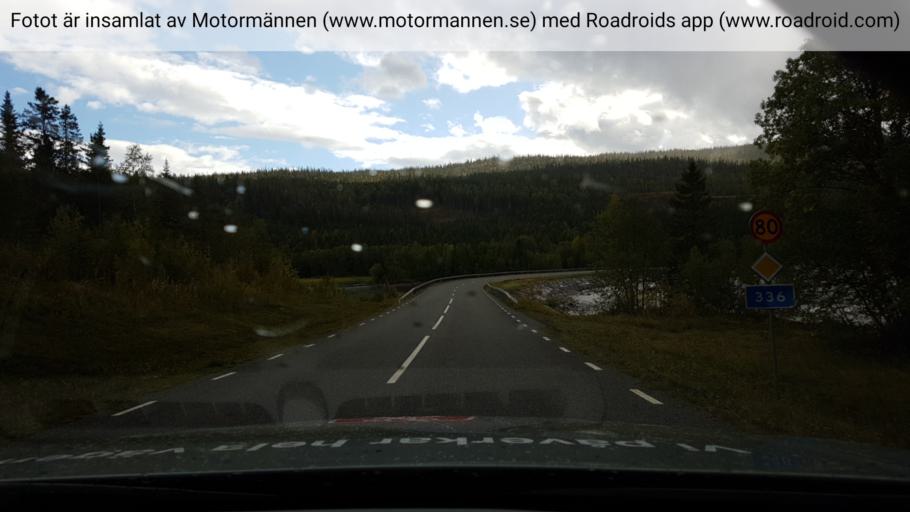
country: SE
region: Jaemtland
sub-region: Are Kommun
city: Are
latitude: 63.6152
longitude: 13.2010
